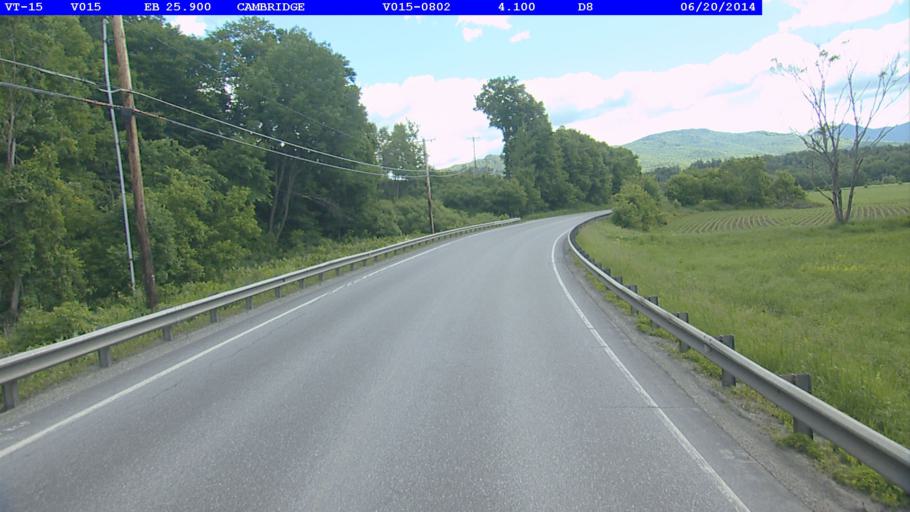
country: US
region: Vermont
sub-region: Lamoille County
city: Johnson
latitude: 44.6457
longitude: -72.8474
